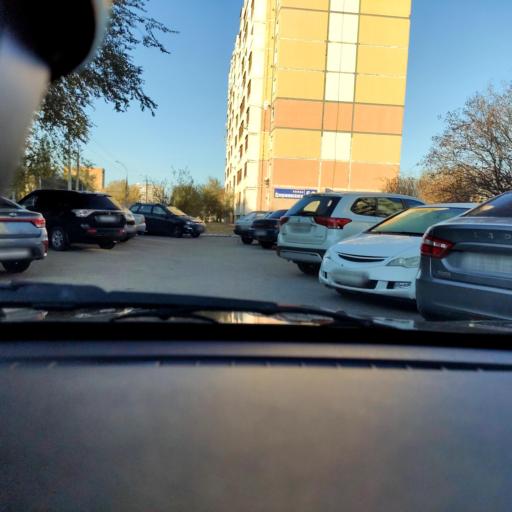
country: RU
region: Samara
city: Tol'yatti
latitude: 53.5357
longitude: 49.3080
